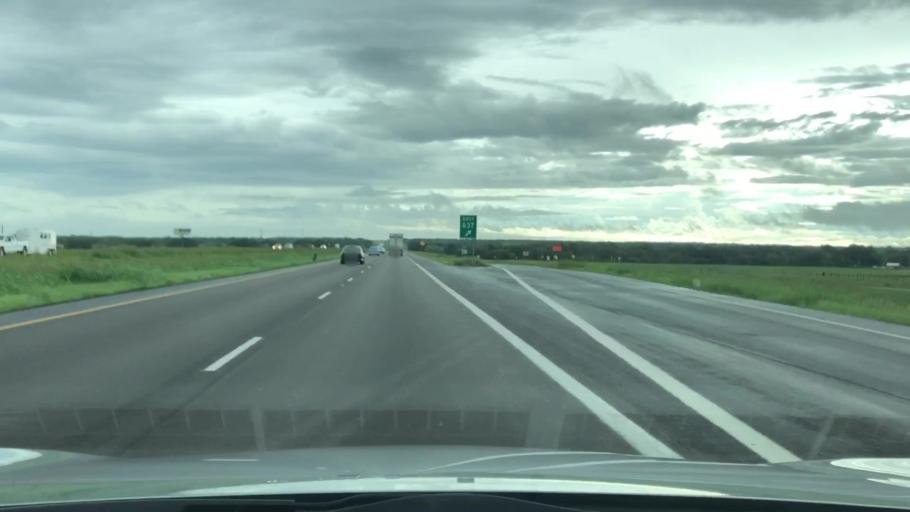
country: US
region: Texas
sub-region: Caldwell County
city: Luling
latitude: 29.6505
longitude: -97.5104
